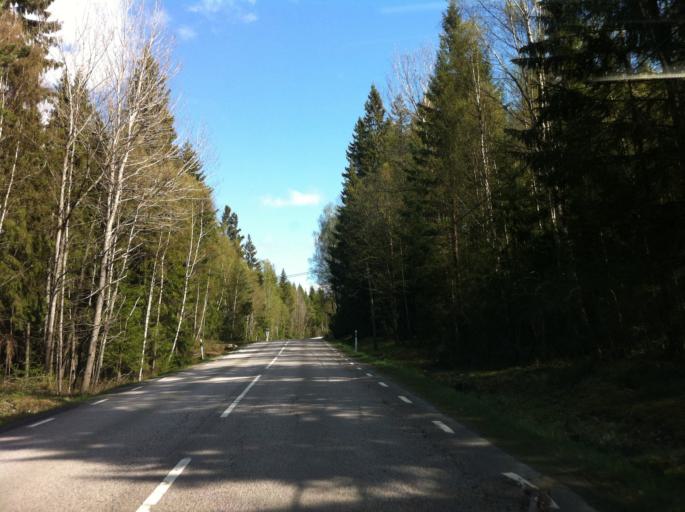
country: SE
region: Vaestra Goetaland
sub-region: Alingsas Kommun
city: Alingsas
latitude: 57.8708
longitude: 12.6001
